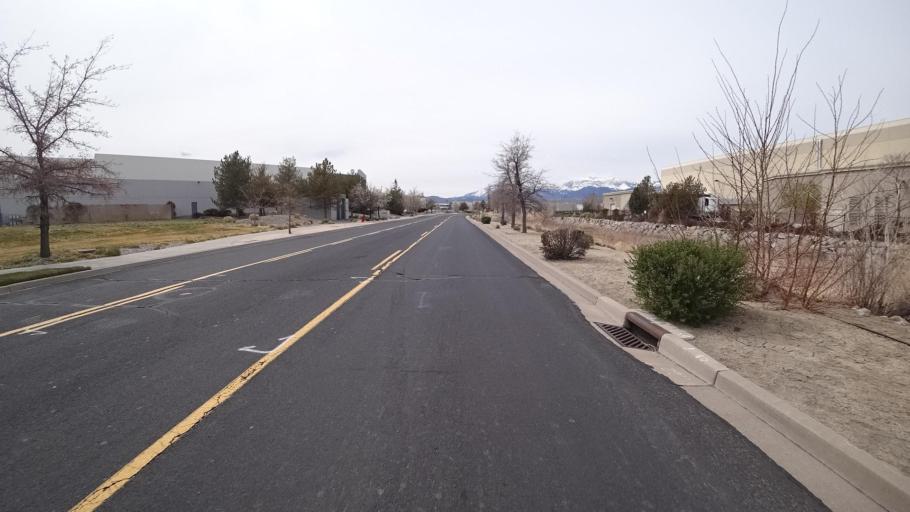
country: US
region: Nevada
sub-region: Washoe County
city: Sparks
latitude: 39.4499
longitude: -119.7474
